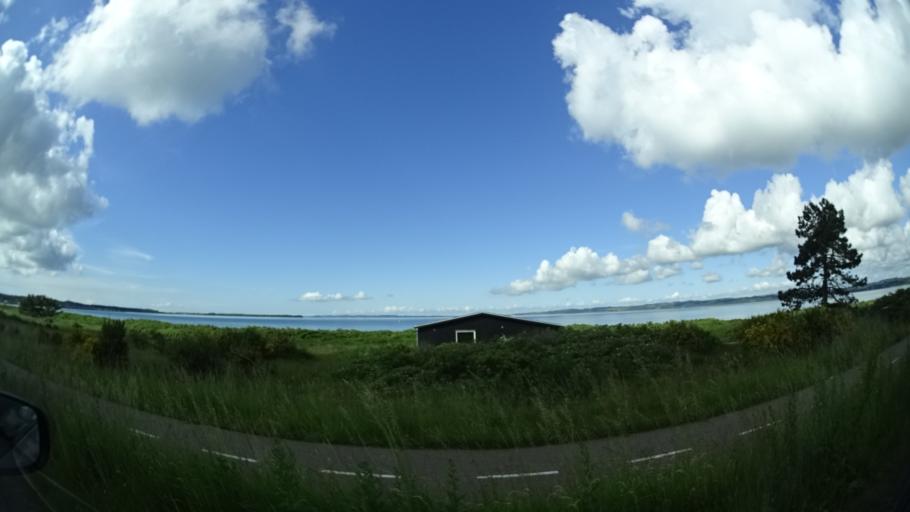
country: DK
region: Central Jutland
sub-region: Syddjurs Kommune
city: Ebeltoft
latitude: 56.2166
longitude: 10.6734
